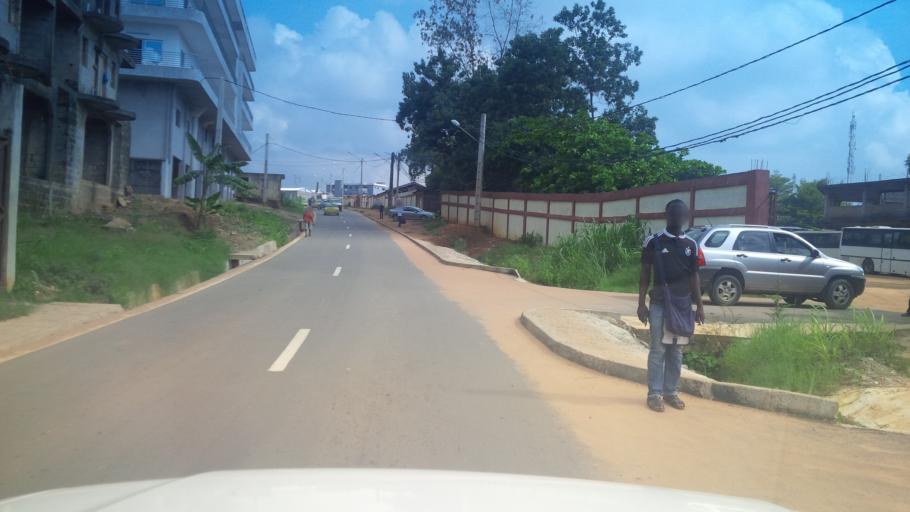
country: CI
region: Lagunes
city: Abobo
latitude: 5.3816
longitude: -3.9548
